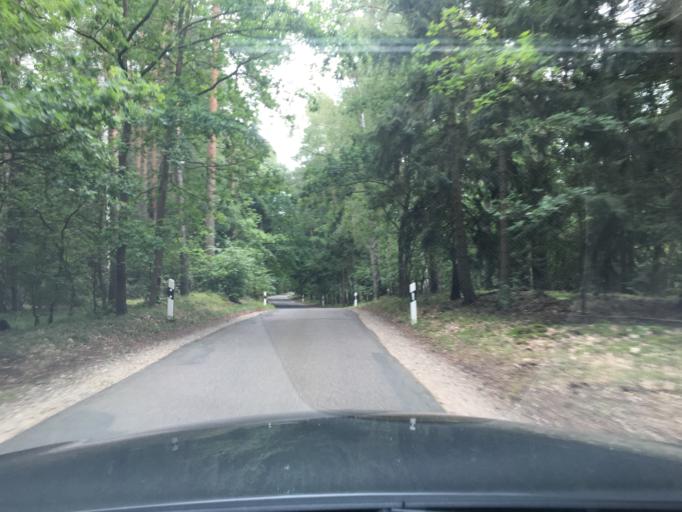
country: DE
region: Mecklenburg-Vorpommern
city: Mollenhagen
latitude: 53.4495
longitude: 12.8223
